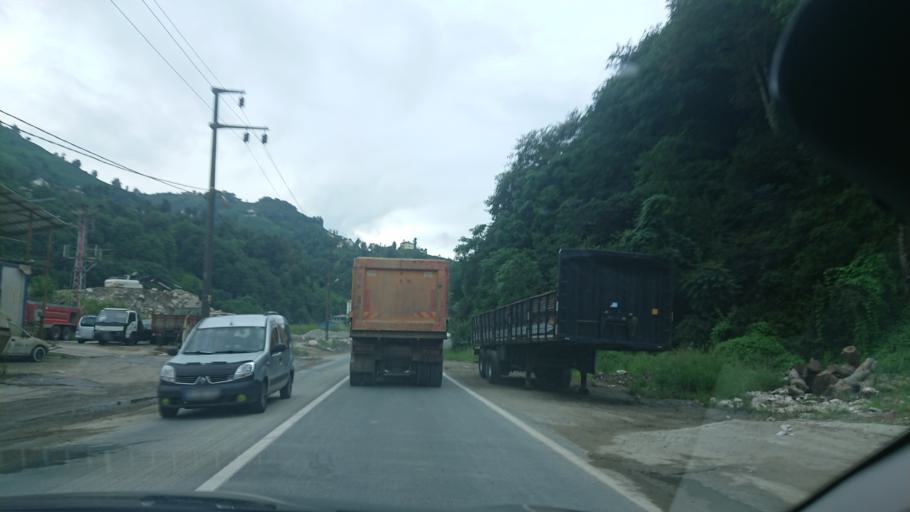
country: TR
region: Rize
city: Gundogdu
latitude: 41.0146
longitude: 40.5669
